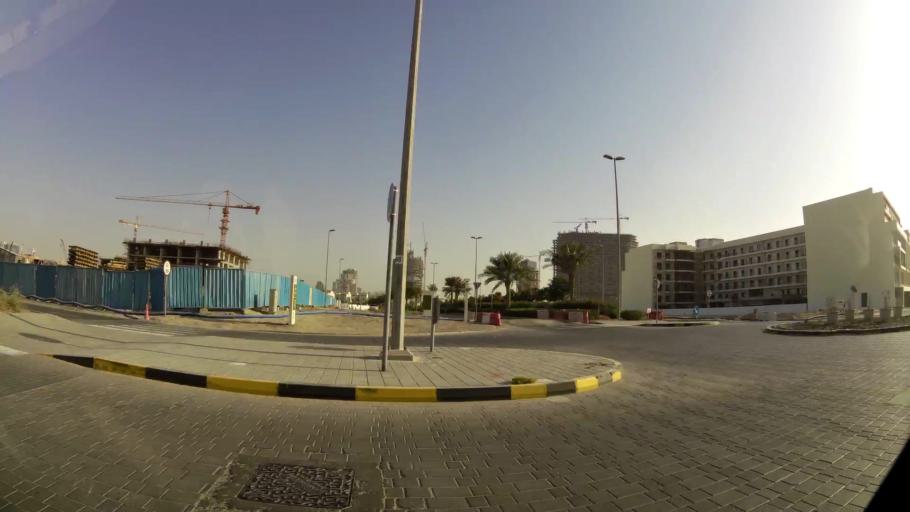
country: AE
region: Dubai
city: Dubai
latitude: 25.0610
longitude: 55.2090
